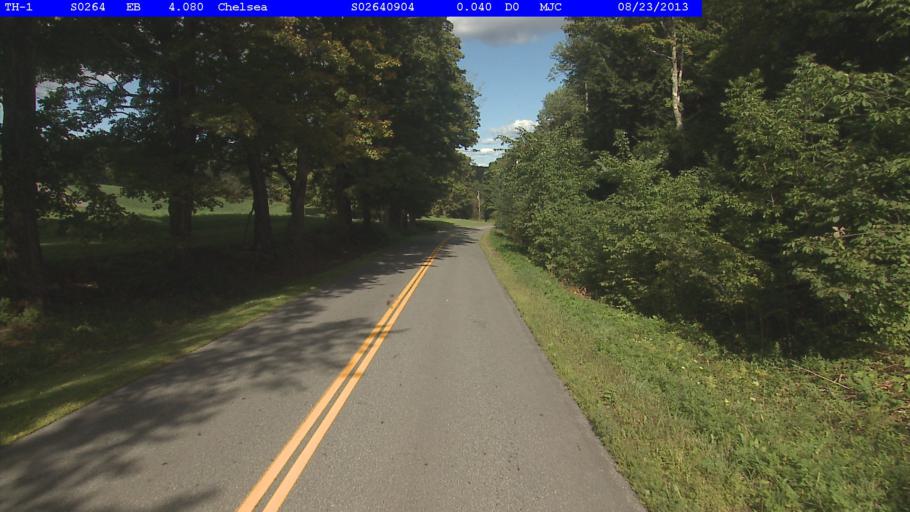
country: US
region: Vermont
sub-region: Orange County
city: Chelsea
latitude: 43.9730
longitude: -72.5115
